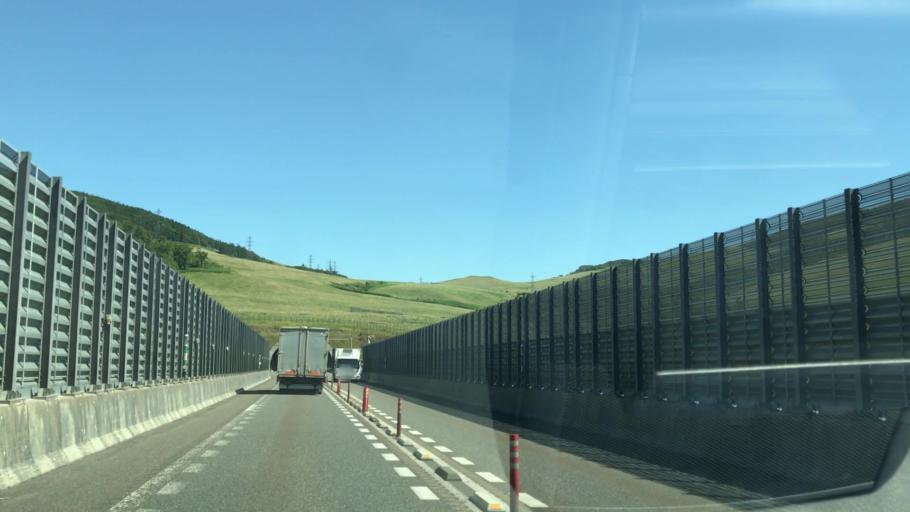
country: JP
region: Hokkaido
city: Shimo-furano
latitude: 43.0606
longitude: 142.7162
